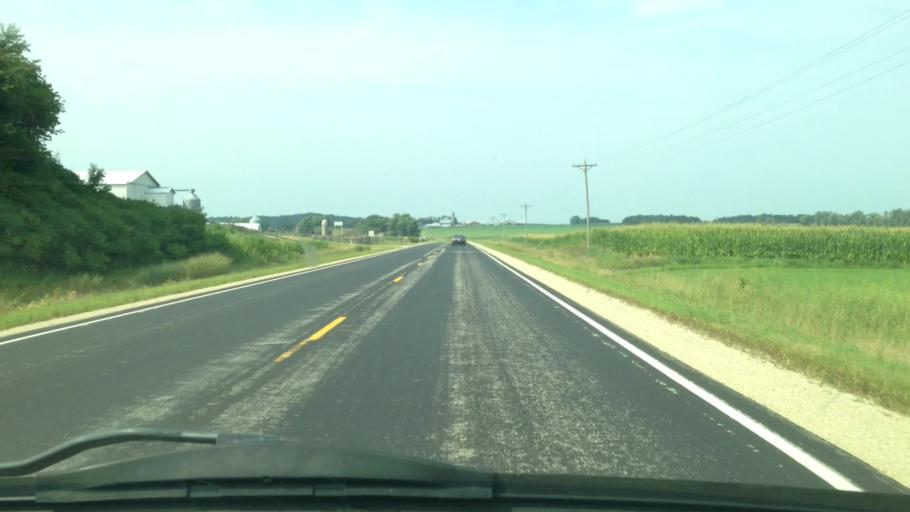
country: US
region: Minnesota
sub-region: Winona County
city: Lewiston
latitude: 43.9439
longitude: -91.9551
